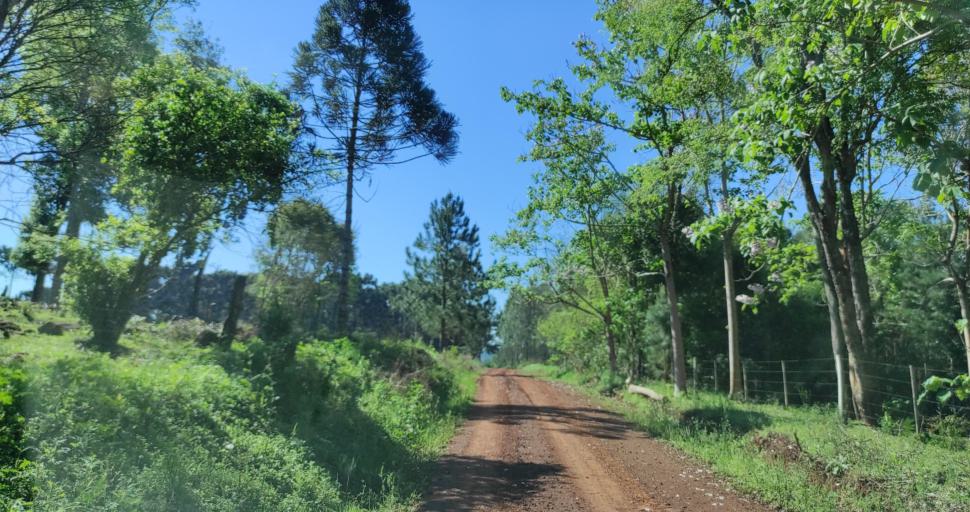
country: AR
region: Misiones
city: Capiovi
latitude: -26.9362
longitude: -55.0017
